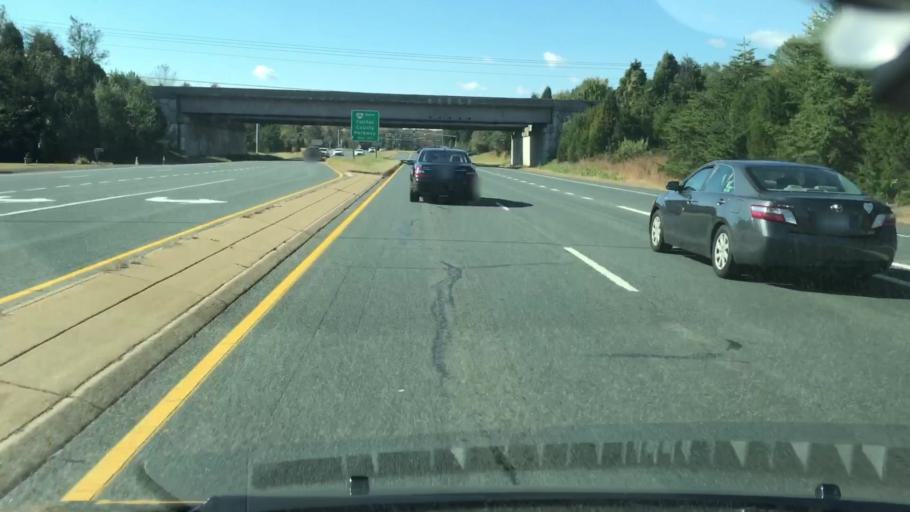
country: US
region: Virginia
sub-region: Fairfax County
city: Fairfax Station
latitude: 38.8293
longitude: -77.3658
